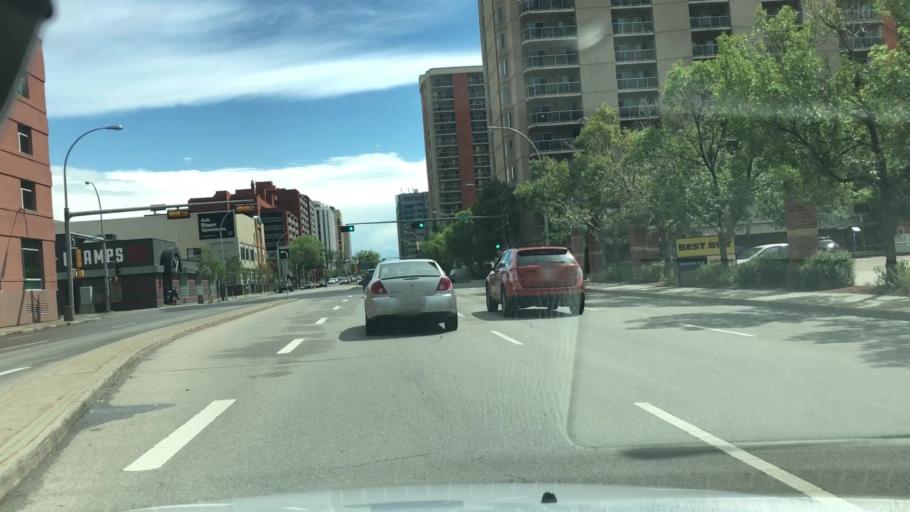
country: CA
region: Alberta
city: Edmonton
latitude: 53.5452
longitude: -113.5086
